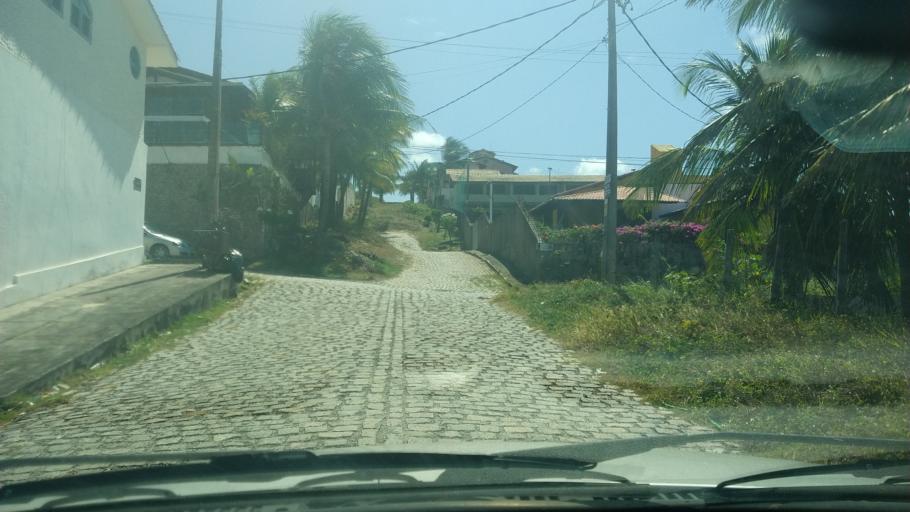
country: BR
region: Rio Grande do Norte
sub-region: Parnamirim
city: Parnamirim
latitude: -5.9485
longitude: -35.1538
